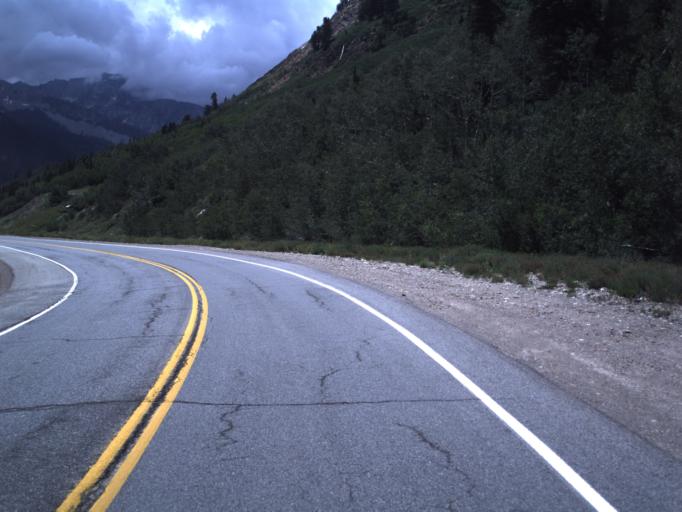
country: US
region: Utah
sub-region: Summit County
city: Snyderville
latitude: 40.5877
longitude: -111.6512
